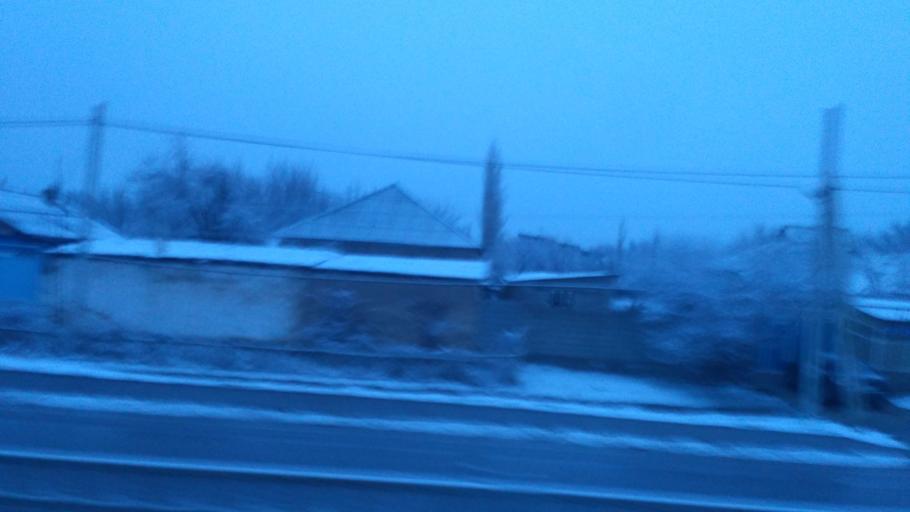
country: KZ
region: Ongtustik Qazaqstan
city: Shymkent
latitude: 42.3777
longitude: 69.4973
